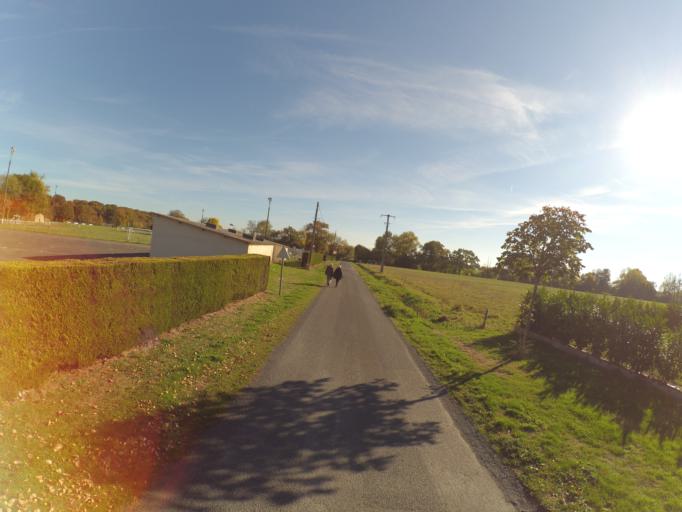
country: FR
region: Pays de la Loire
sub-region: Departement de la Loire-Atlantique
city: Saint-Lumine-de-Clisson
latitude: 47.0853
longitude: -1.3302
